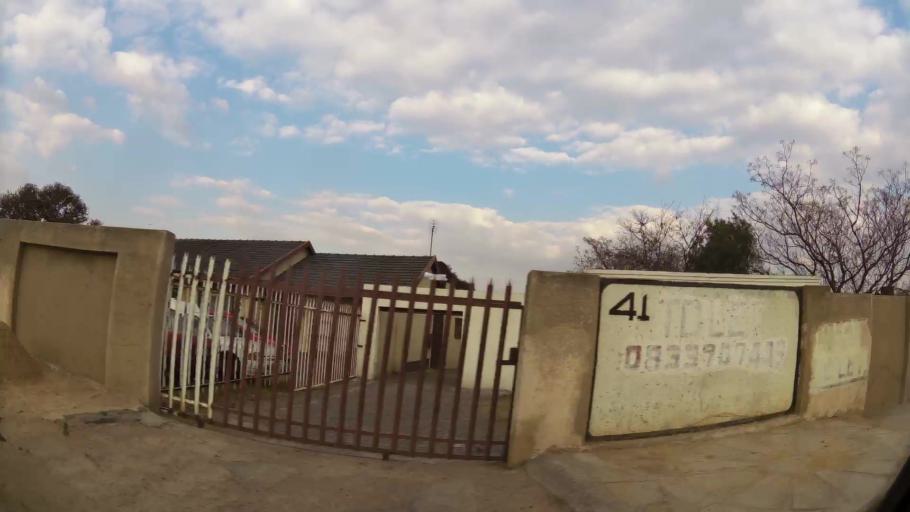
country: ZA
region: Gauteng
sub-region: Ekurhuleni Metropolitan Municipality
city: Germiston
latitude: -26.2394
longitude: 28.1954
